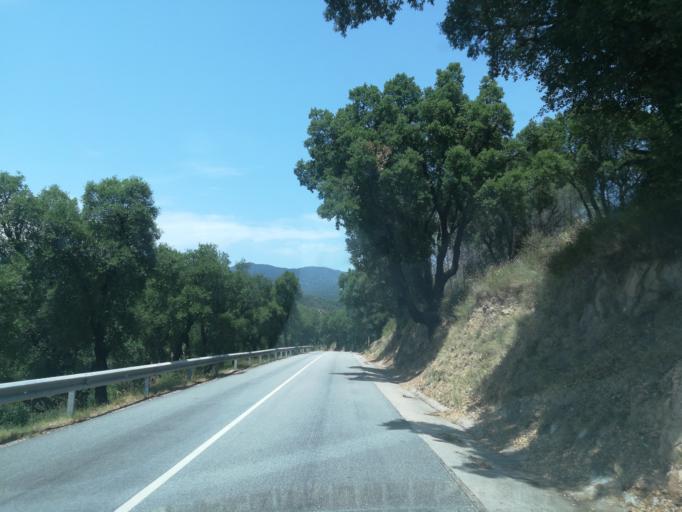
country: ES
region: Catalonia
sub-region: Provincia de Girona
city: Agullana
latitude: 42.3950
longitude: 2.8506
